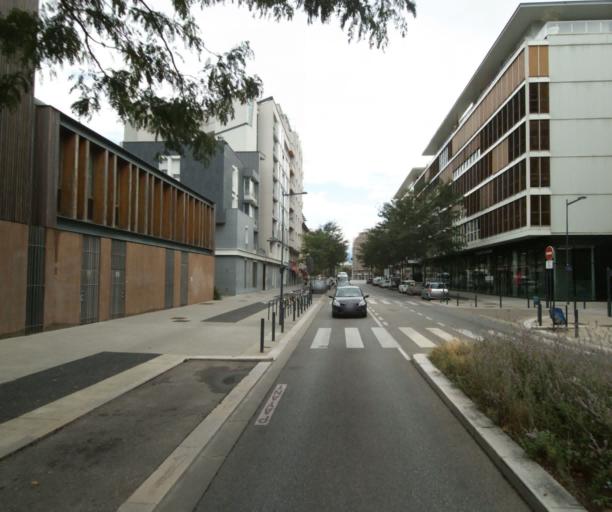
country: FR
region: Rhone-Alpes
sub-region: Departement de l'Isere
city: Grenoble
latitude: 45.1836
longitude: 5.7264
